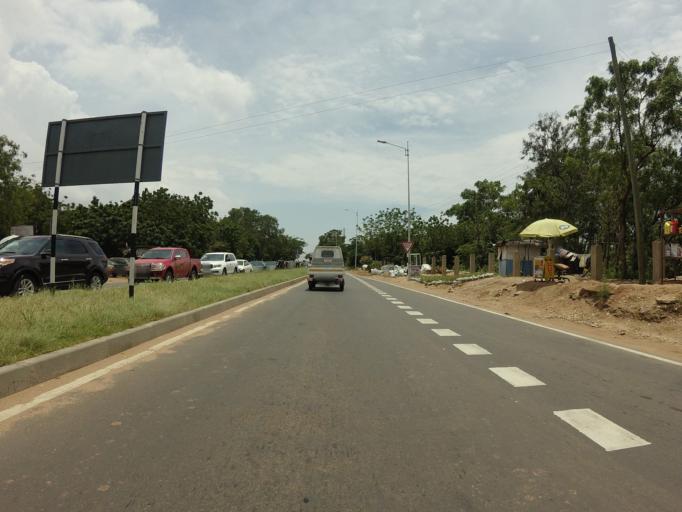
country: GH
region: Greater Accra
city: Medina Estates
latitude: 5.6307
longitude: -0.1556
